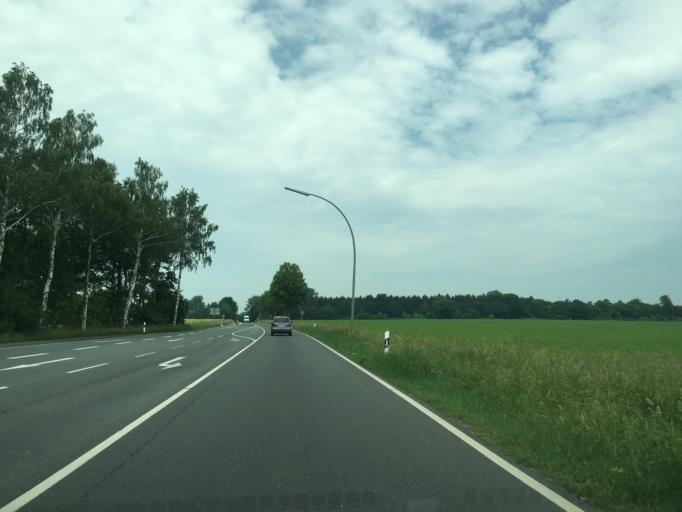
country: DE
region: North Rhine-Westphalia
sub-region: Regierungsbezirk Munster
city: Steinfurt
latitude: 52.1279
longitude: 7.3899
